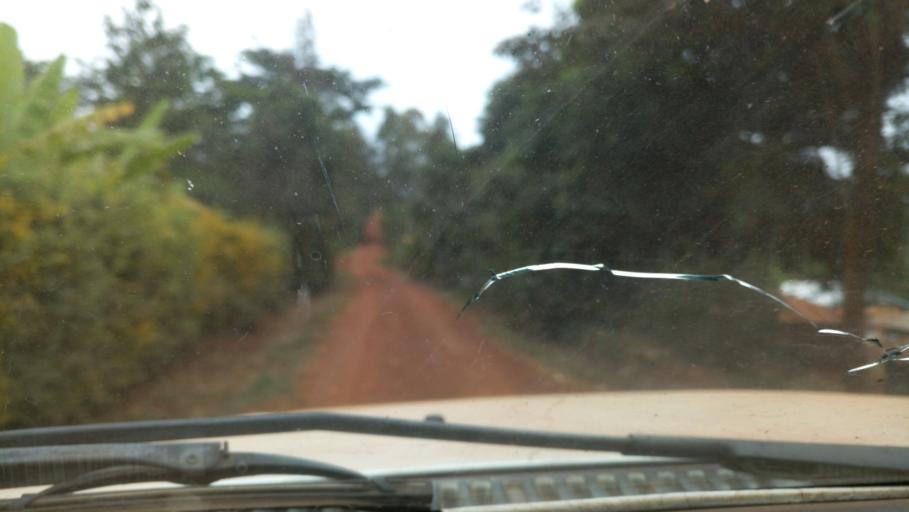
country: KE
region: Murang'a District
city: Maragua
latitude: -0.7693
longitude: 37.0809
